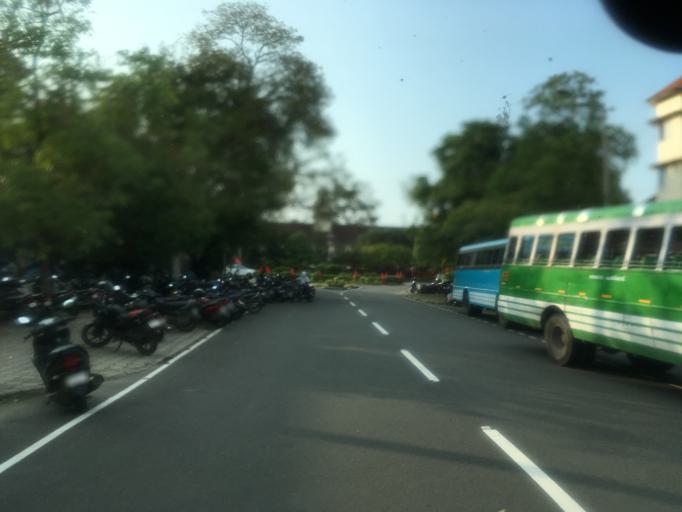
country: IN
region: Kerala
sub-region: Ernakulam
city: Cochin
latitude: 9.9689
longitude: 76.2597
